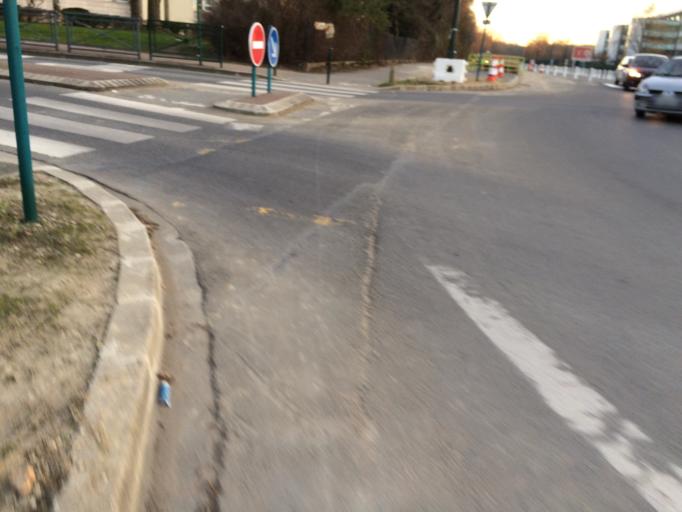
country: FR
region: Ile-de-France
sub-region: Departement des Hauts-de-Seine
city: Chatenay-Malabry
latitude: 48.7765
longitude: 2.2501
